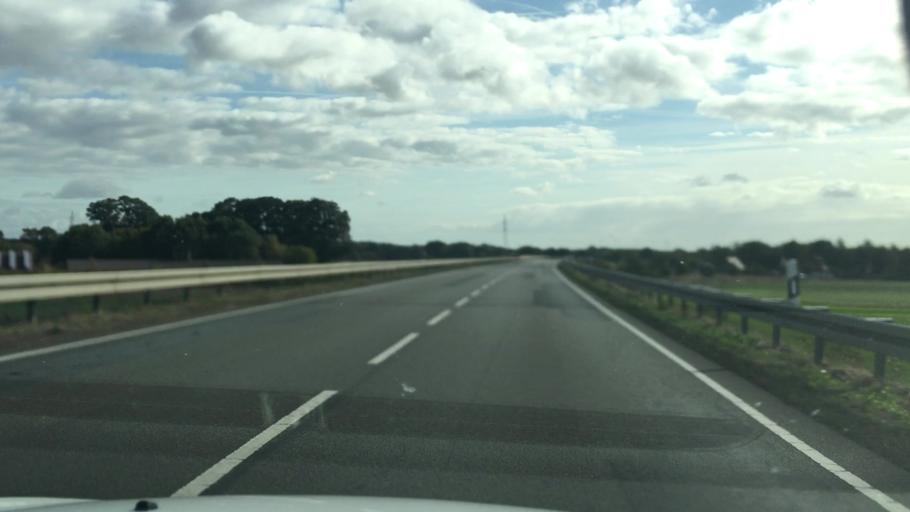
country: DE
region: Lower Saxony
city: Wetschen
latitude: 52.6228
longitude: 8.4115
